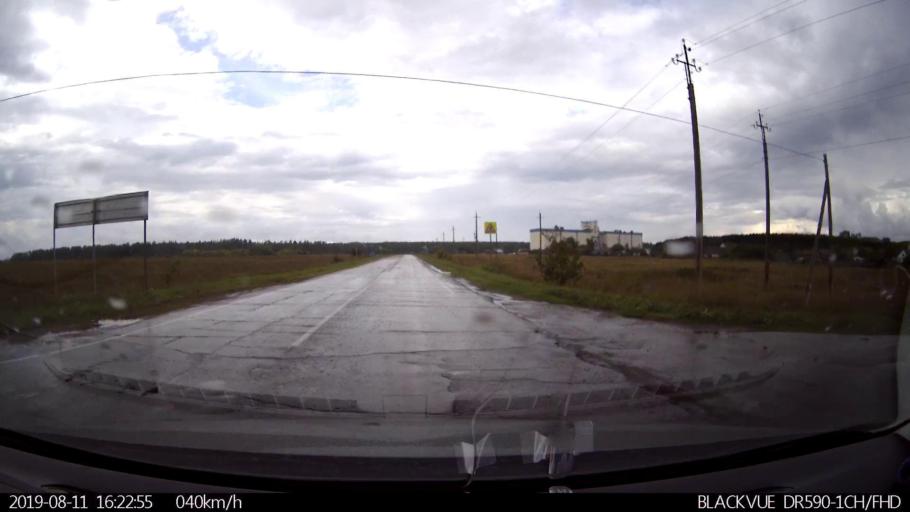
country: RU
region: Ulyanovsk
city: Mayna
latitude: 54.0916
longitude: 47.5907
